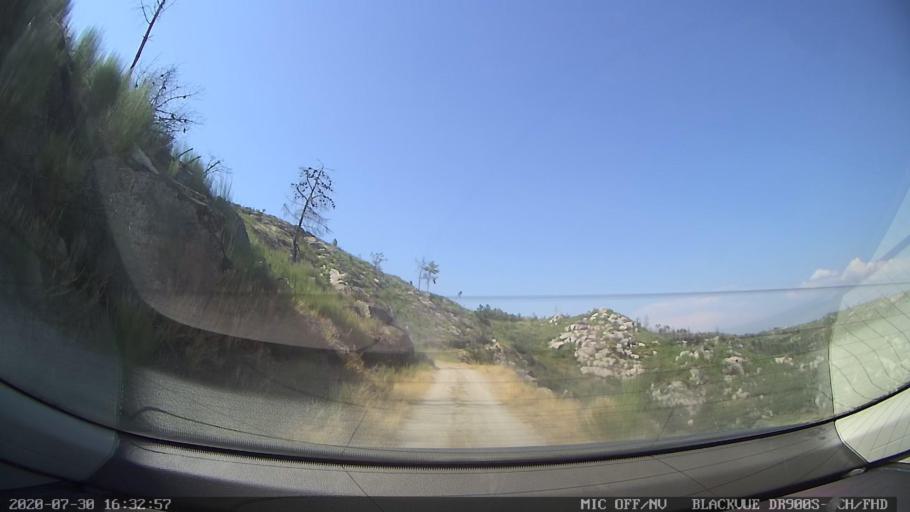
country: PT
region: Vila Real
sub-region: Sabrosa
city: Sabrosa
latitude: 41.3105
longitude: -7.4918
